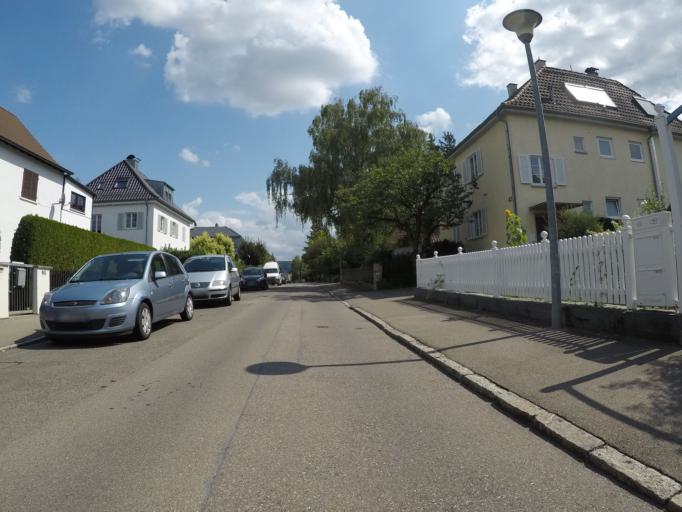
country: DE
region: Baden-Wuerttemberg
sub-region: Tuebingen Region
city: Reutlingen
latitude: 48.4883
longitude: 9.1977
